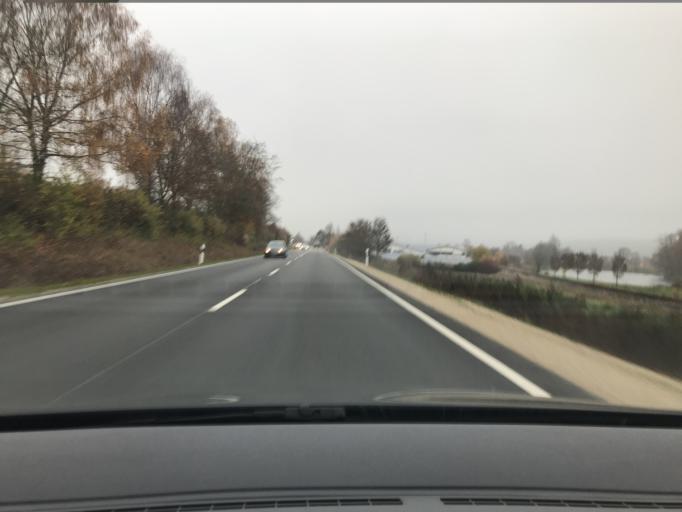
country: DE
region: Bavaria
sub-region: Regierungsbezirk Mittelfranken
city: Wilburgstetten
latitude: 49.0182
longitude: 10.4009
